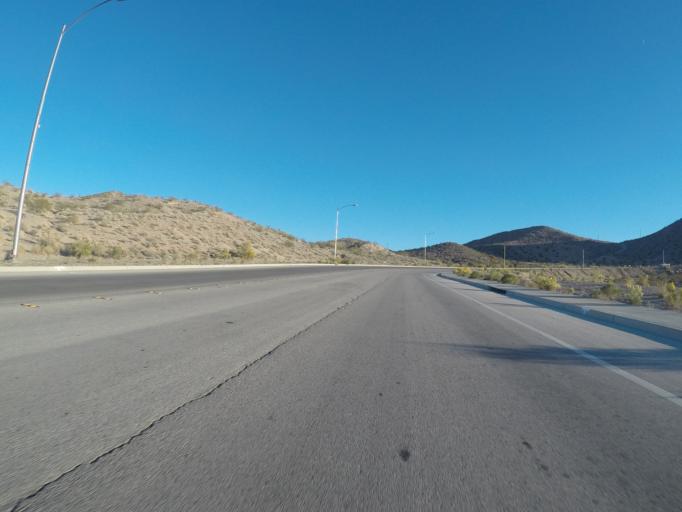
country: US
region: Nevada
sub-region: Clark County
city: Boulder City
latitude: 35.9842
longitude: -114.8283
